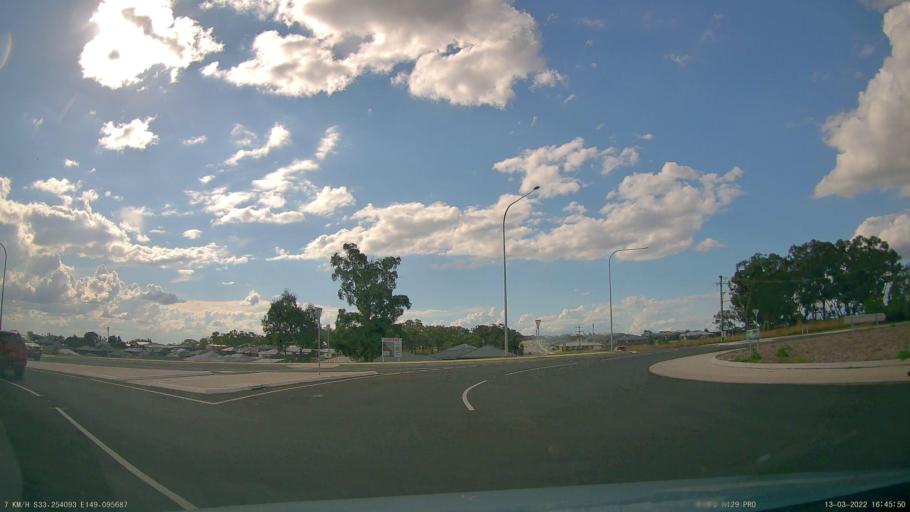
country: AU
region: New South Wales
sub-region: Orange Municipality
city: Orange
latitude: -33.2541
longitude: 149.0958
